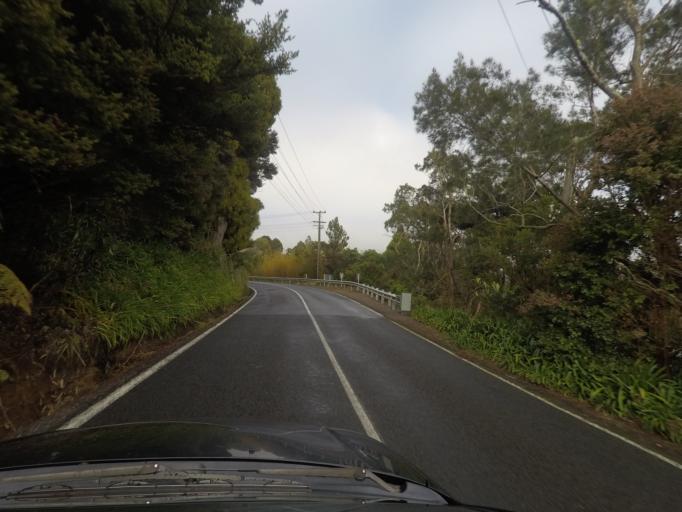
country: NZ
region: Auckland
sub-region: Auckland
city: Titirangi
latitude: -36.9208
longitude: 174.5848
